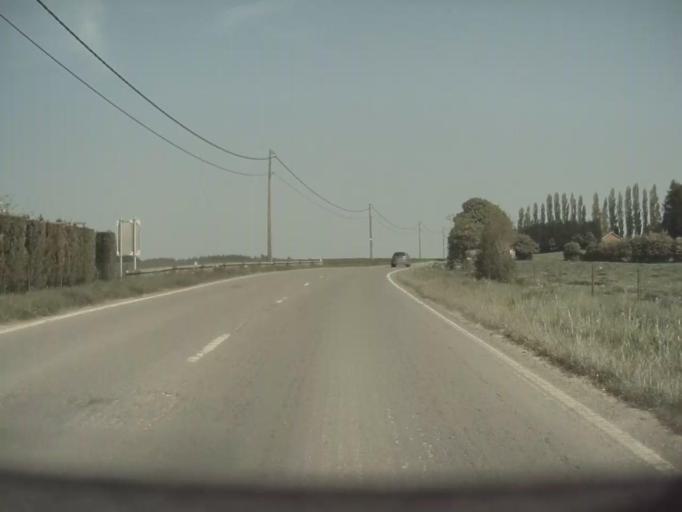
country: BE
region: Wallonia
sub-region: Province de Namur
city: Dinant
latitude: 50.2640
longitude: 4.9575
